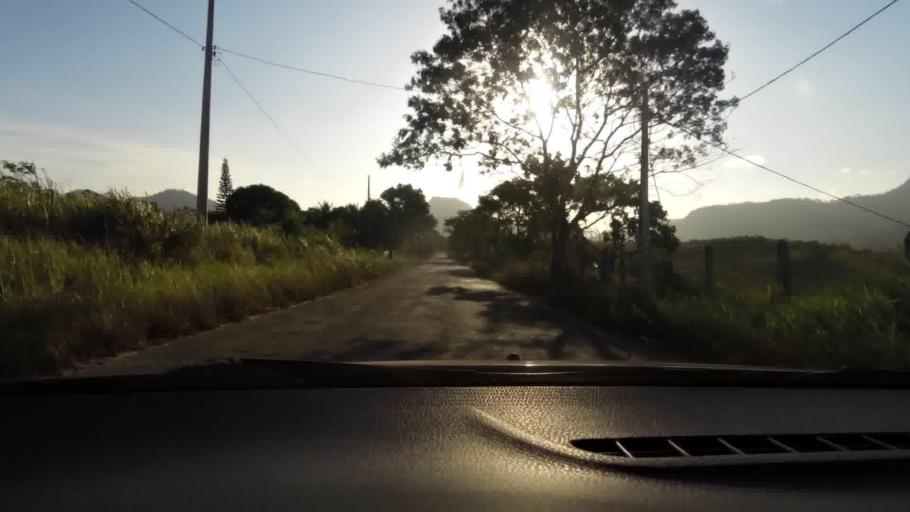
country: BR
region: Espirito Santo
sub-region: Guarapari
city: Guarapari
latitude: -20.5308
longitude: -40.4653
